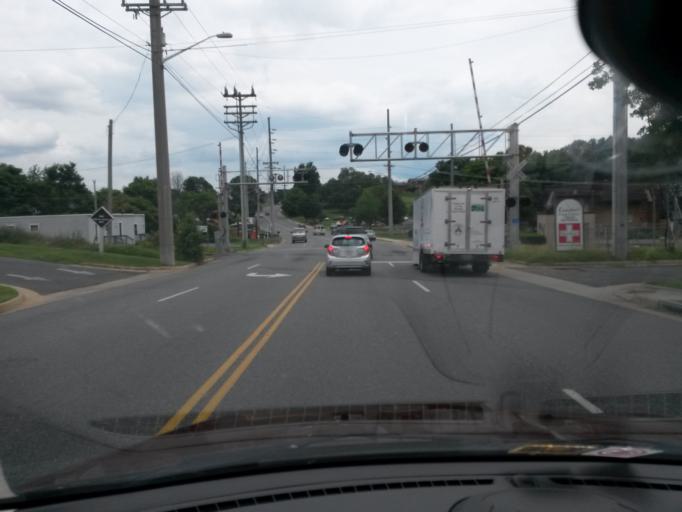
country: US
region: Virginia
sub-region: City of Harrisonburg
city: Harrisonburg
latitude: 38.4403
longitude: -78.8568
